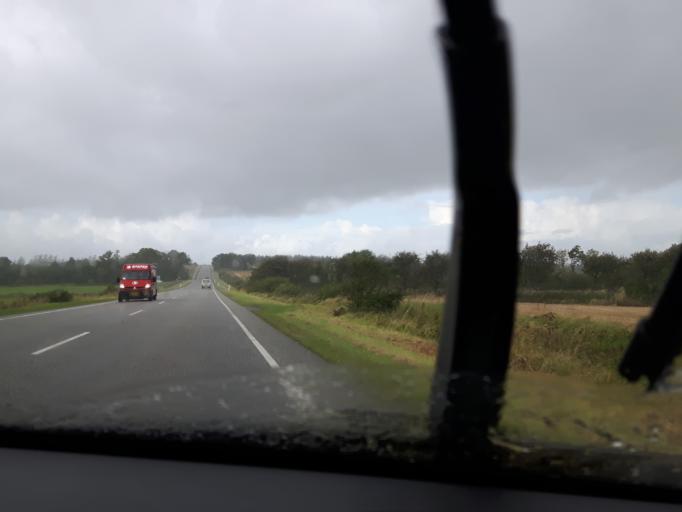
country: DK
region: North Denmark
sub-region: Jammerbugt Kommune
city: Fjerritslev
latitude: 57.0878
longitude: 9.3215
